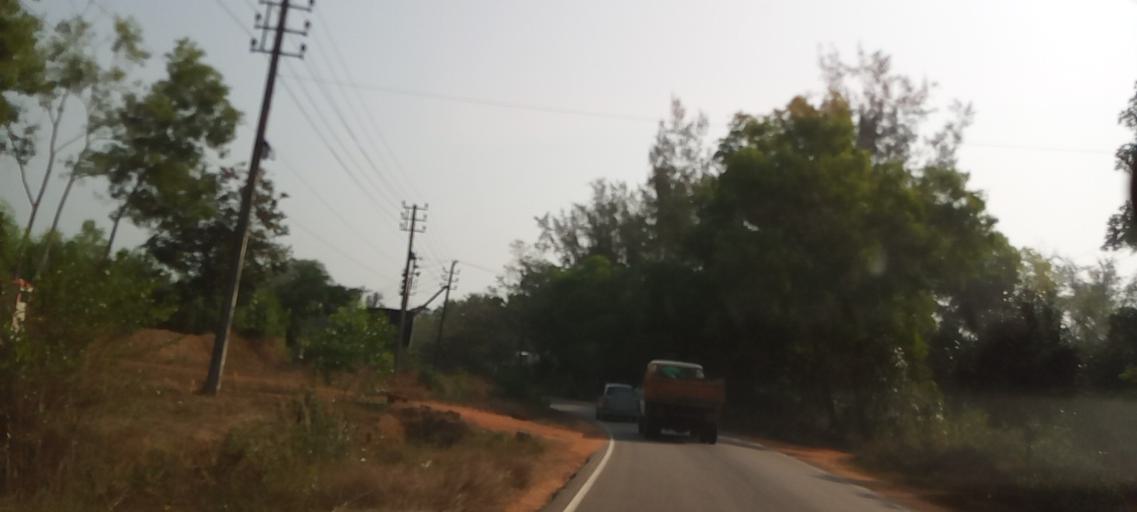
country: IN
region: Karnataka
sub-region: Udupi
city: Coondapoor
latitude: 13.5142
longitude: 74.7415
